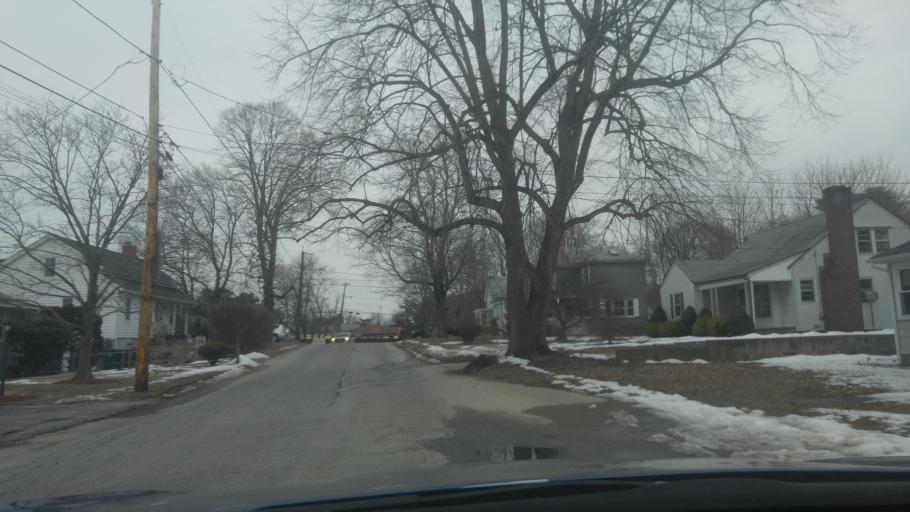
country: US
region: Rhode Island
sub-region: Kent County
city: West Warwick
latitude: 41.6841
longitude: -71.5655
